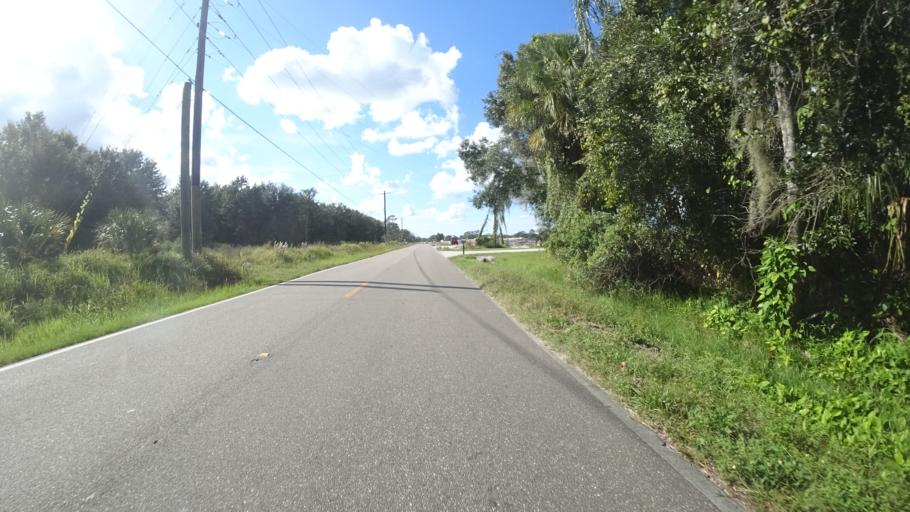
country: US
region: Florida
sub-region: Manatee County
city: Ellenton
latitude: 27.5539
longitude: -82.3907
